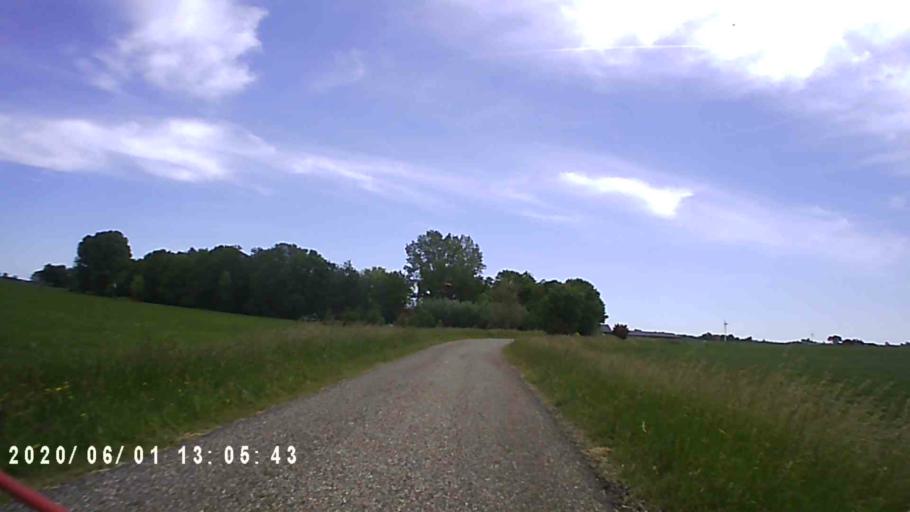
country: NL
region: Friesland
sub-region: Gemeente Franekeradeel
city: Tzum
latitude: 53.1363
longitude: 5.5487
